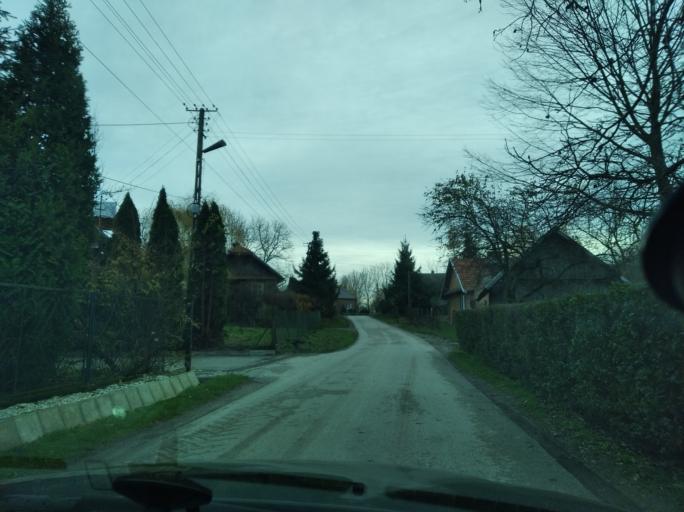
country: PL
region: Subcarpathian Voivodeship
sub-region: Powiat przeworski
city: Debow
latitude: 50.0472
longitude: 22.4499
